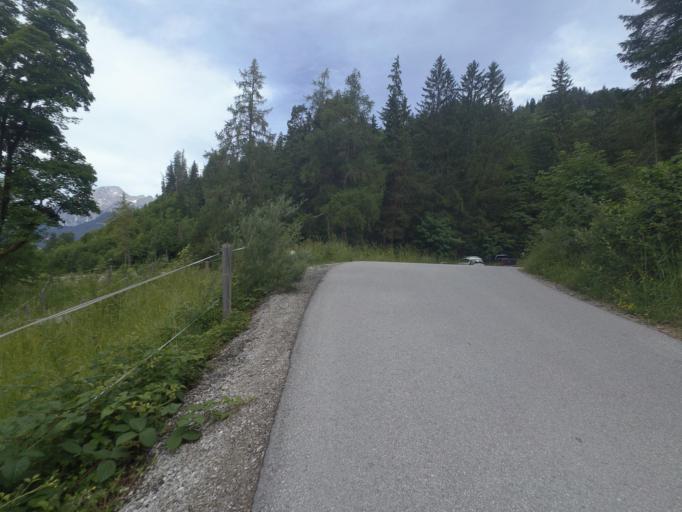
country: AT
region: Salzburg
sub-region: Politischer Bezirk Zell am See
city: Saalfelden am Steinernen Meer
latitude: 47.4391
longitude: 12.8620
